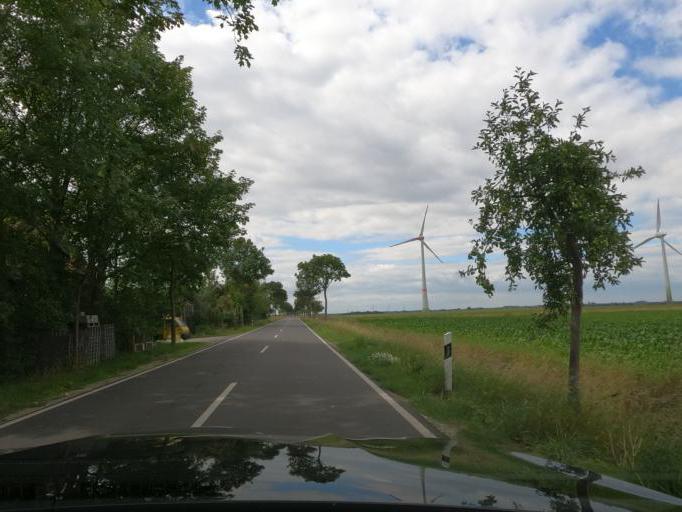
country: DE
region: Lower Saxony
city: Schellerten
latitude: 52.2267
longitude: 10.1193
